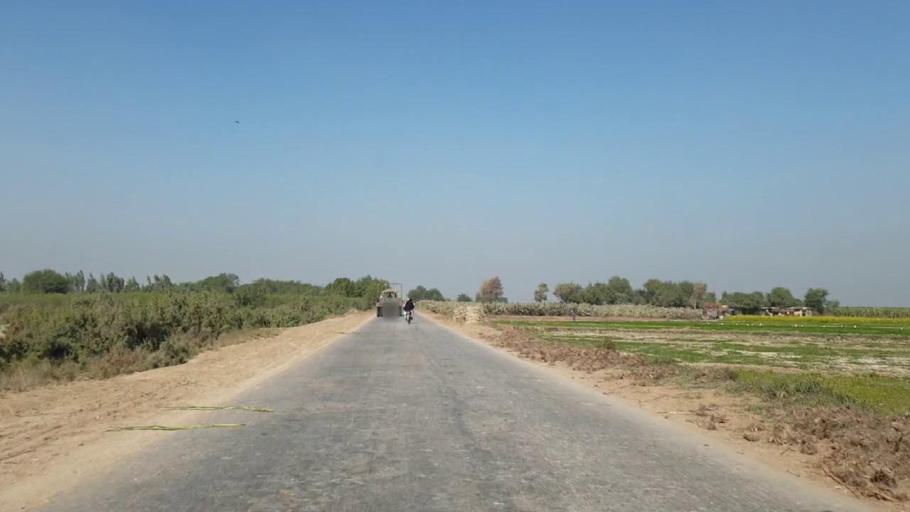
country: PK
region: Sindh
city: Tando Adam
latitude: 25.6574
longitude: 68.5860
